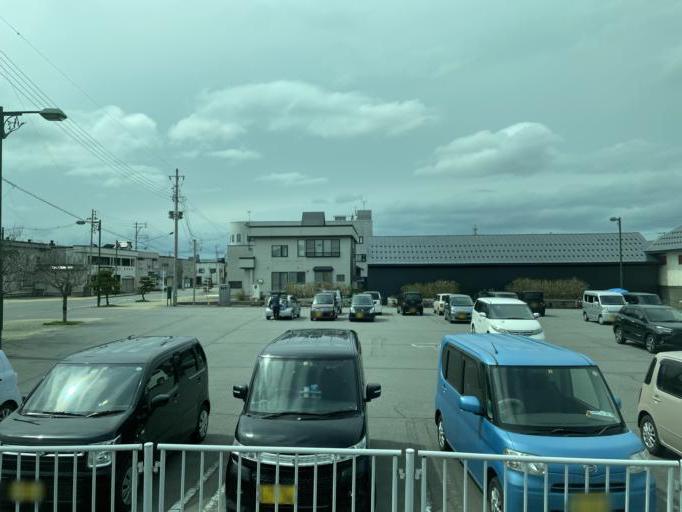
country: JP
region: Aomori
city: Goshogawara
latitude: 40.7582
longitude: 140.4355
